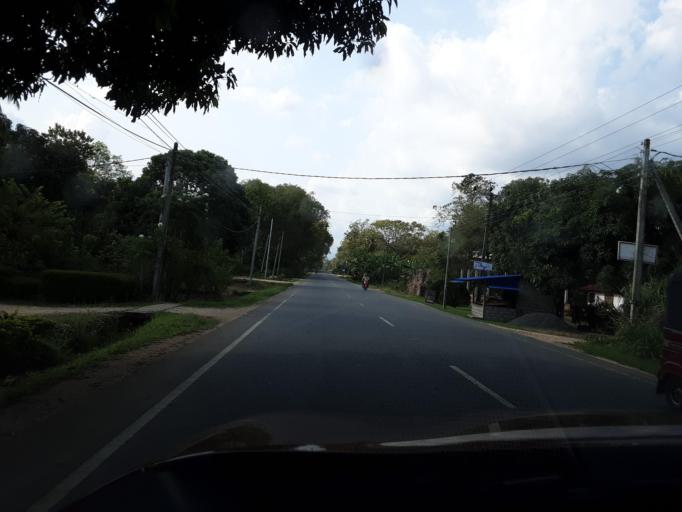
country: LK
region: Uva
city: Haputale
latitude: 6.6638
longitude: 81.1140
